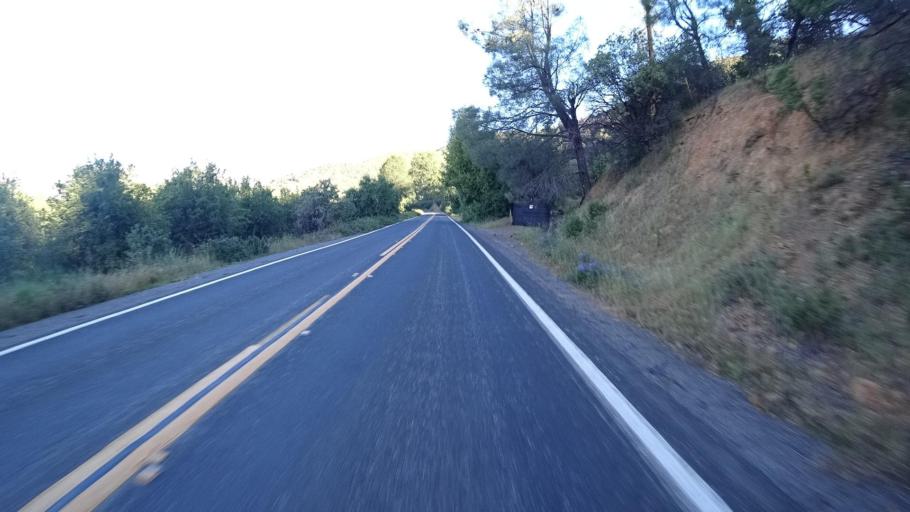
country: US
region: California
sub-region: Lake County
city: Upper Lake
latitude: 39.2076
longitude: -122.9084
